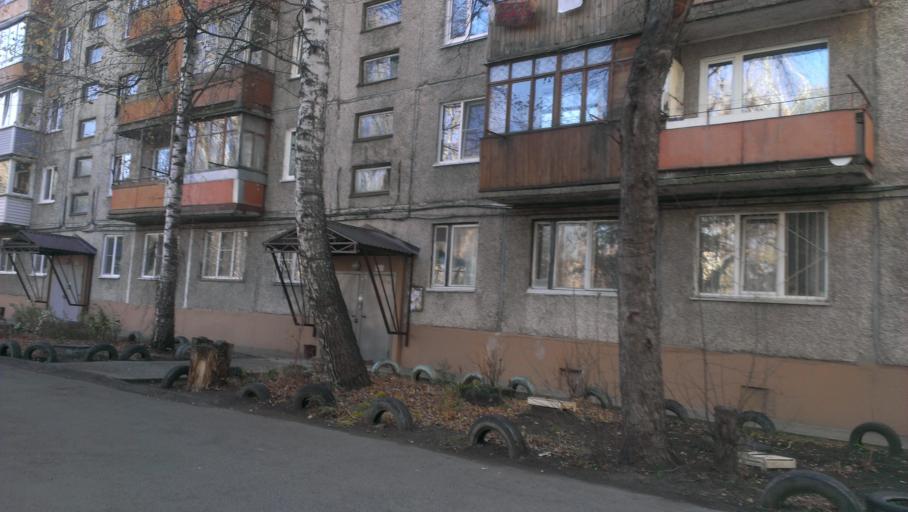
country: RU
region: Altai Krai
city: Novosilikatnyy
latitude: 53.3465
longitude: 83.6856
